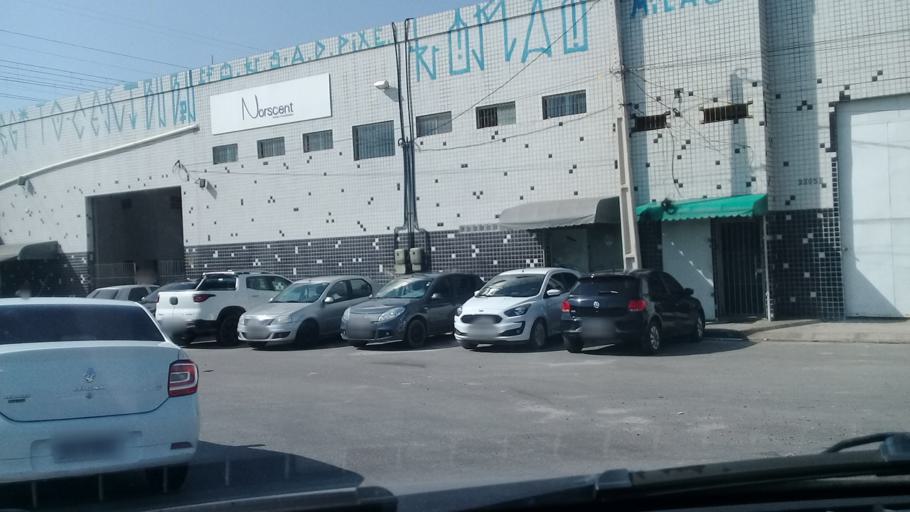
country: BR
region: Pernambuco
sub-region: Jaboatao Dos Guararapes
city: Jaboatao
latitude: -8.1441
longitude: -34.9174
